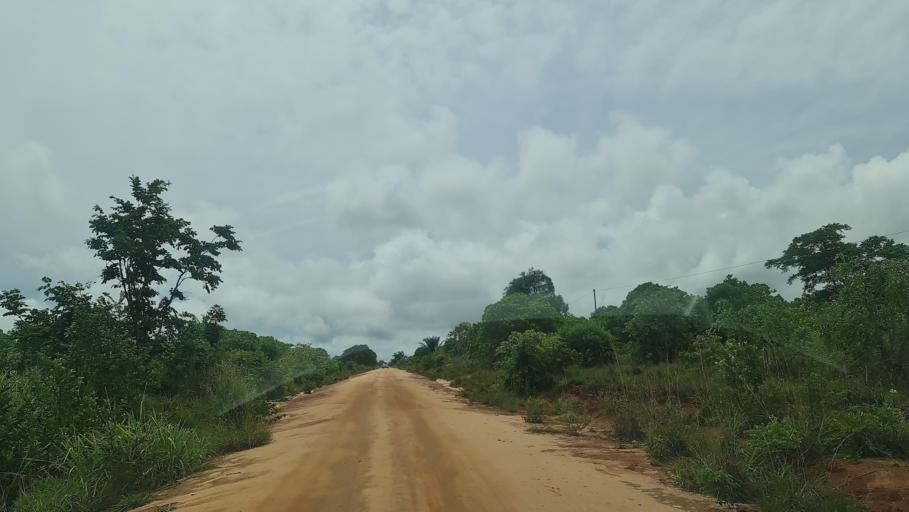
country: MZ
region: Zambezia
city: Quelimane
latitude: -17.2487
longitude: 37.2149
